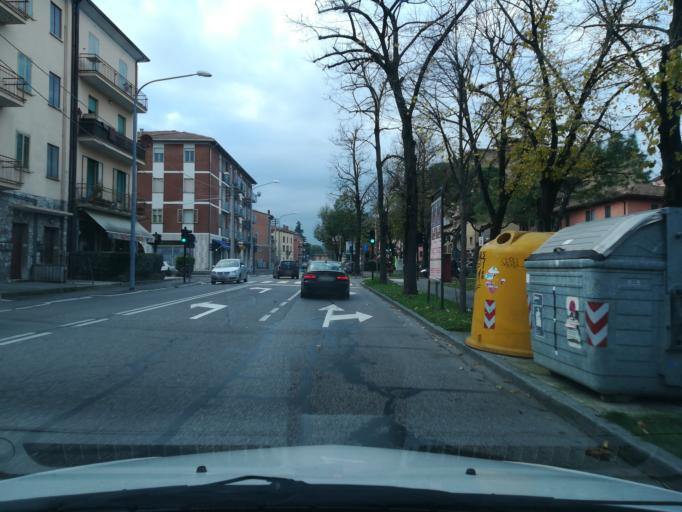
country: IT
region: Emilia-Romagna
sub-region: Provincia di Bologna
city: Imola
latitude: 44.3529
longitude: 11.7208
